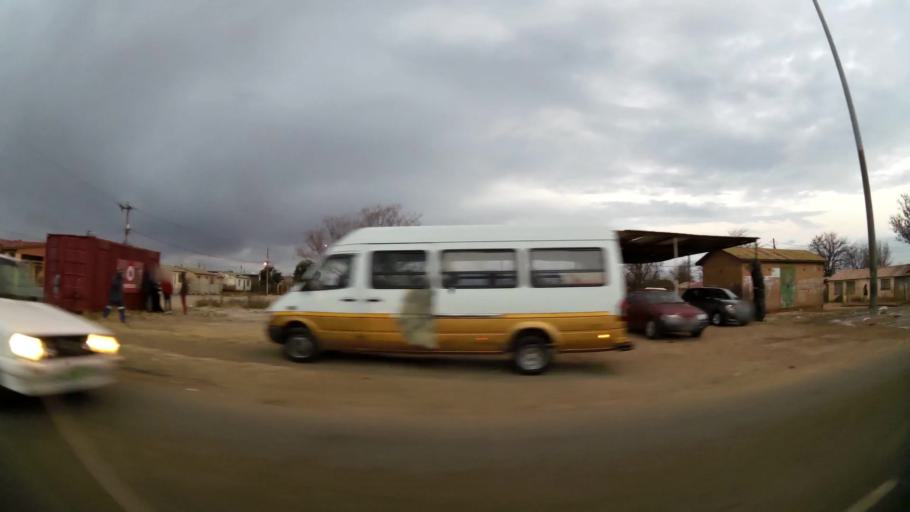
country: ZA
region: Orange Free State
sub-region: Lejweleputswa District Municipality
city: Welkom
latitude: -27.9728
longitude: 26.7859
